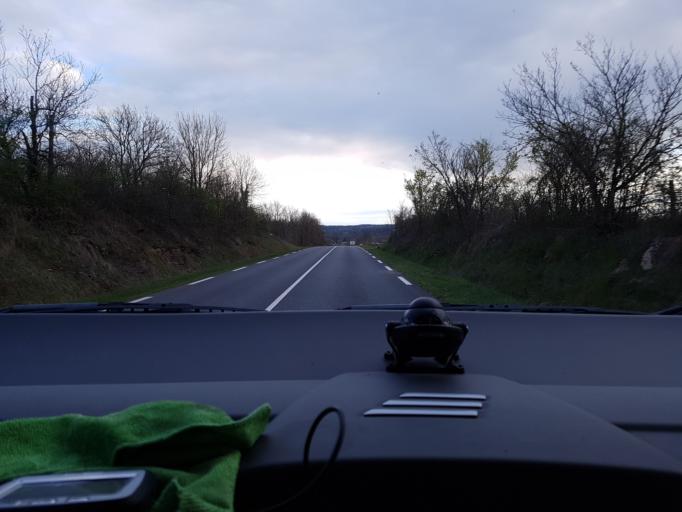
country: FR
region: Midi-Pyrenees
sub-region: Departement de l'Aveyron
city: Bozouls
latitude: 44.4798
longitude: 2.7336
